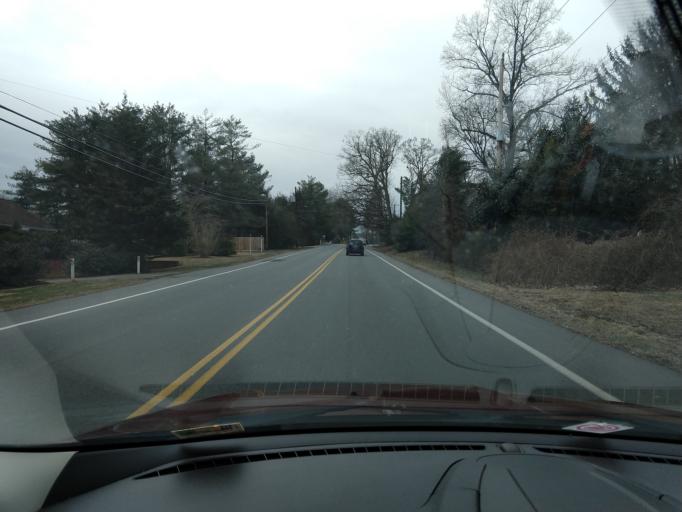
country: US
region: Virginia
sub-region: City of Waynesboro
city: Waynesboro
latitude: 38.0695
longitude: -78.9149
